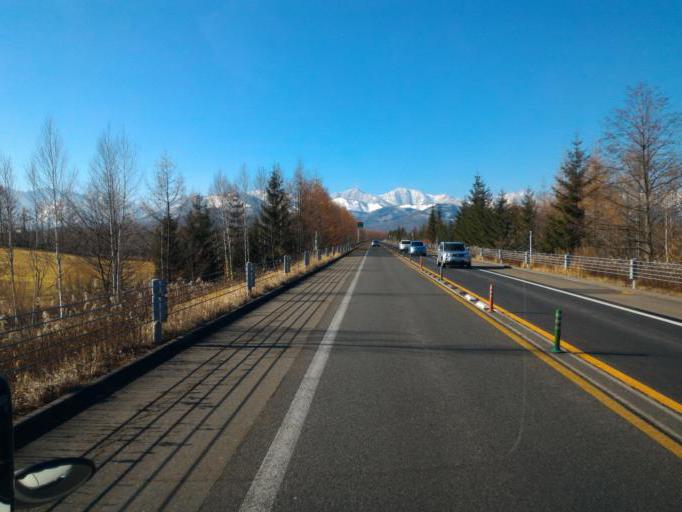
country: JP
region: Hokkaido
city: Otofuke
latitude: 42.9732
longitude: 142.9076
